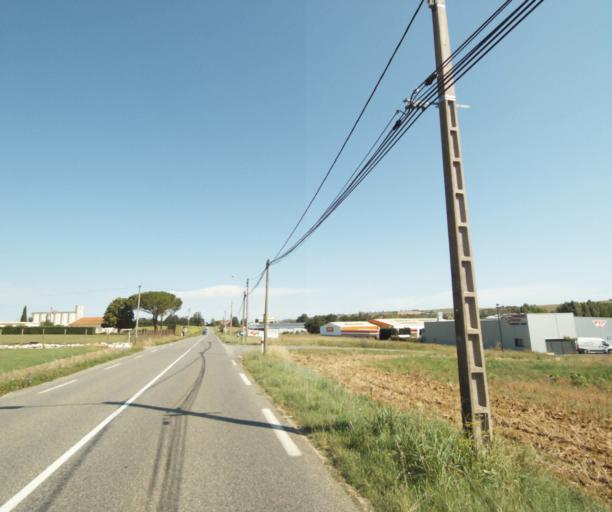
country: FR
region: Midi-Pyrenees
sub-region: Departement de l'Ariege
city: Lezat-sur-Leze
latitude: 43.2847
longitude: 1.3462
